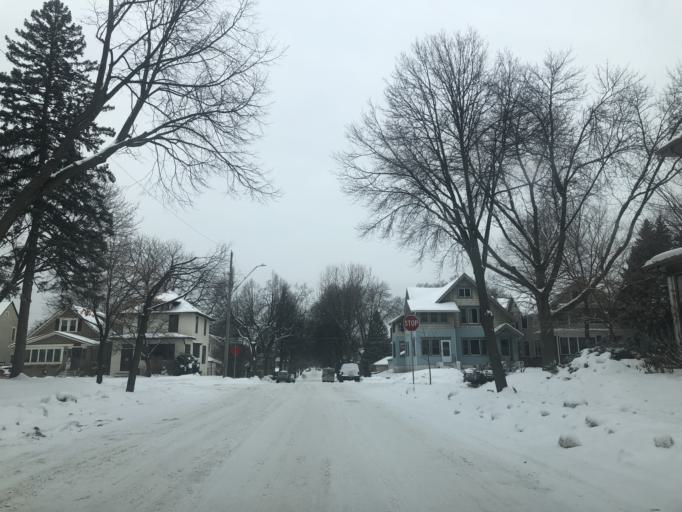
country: US
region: Minnesota
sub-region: Hennepin County
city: Richfield
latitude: 44.9287
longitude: -93.2813
